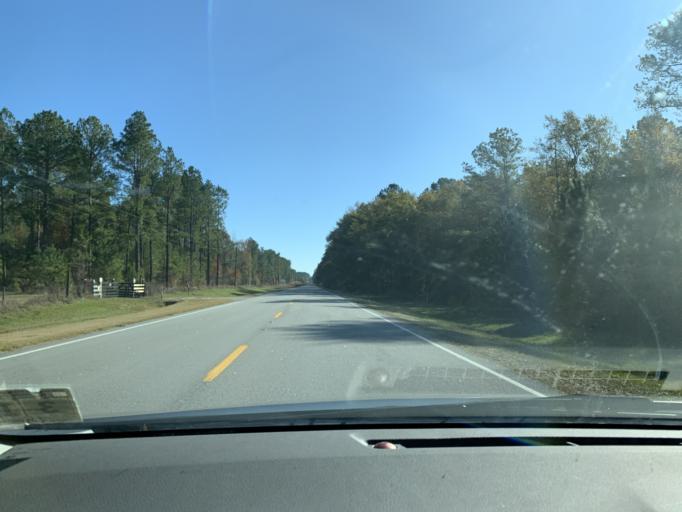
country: US
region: Georgia
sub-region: Ben Hill County
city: Fitzgerald
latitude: 31.7757
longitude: -83.0651
